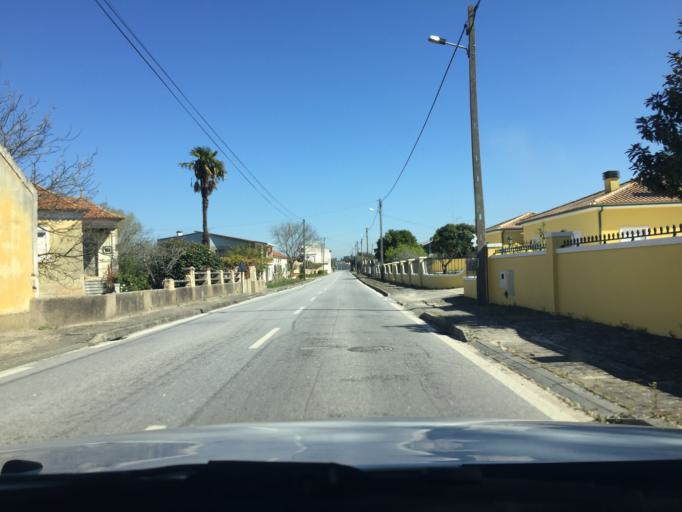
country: PT
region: Aveiro
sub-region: Anadia
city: Sangalhos
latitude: 40.4281
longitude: -8.5136
